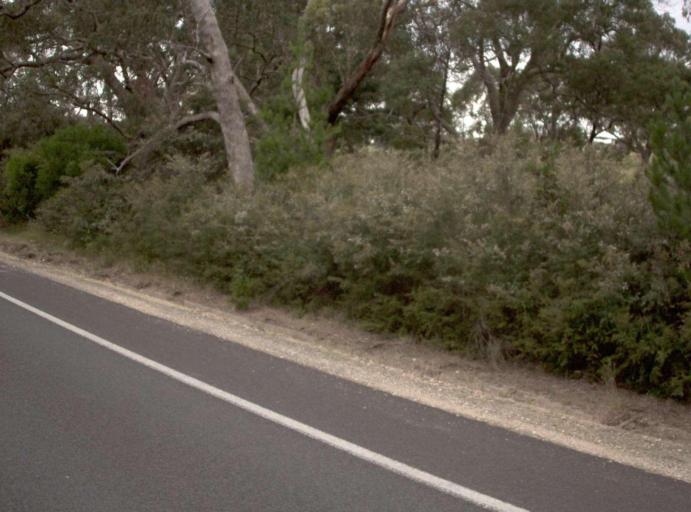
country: AU
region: Victoria
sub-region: Wellington
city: Sale
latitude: -38.1870
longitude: 147.0807
